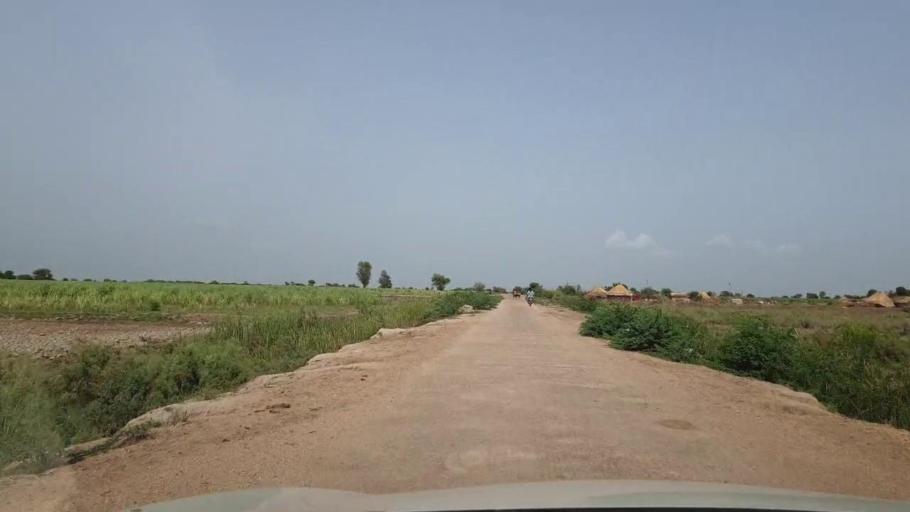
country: PK
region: Sindh
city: Mirwah Gorchani
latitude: 25.2560
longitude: 68.9618
